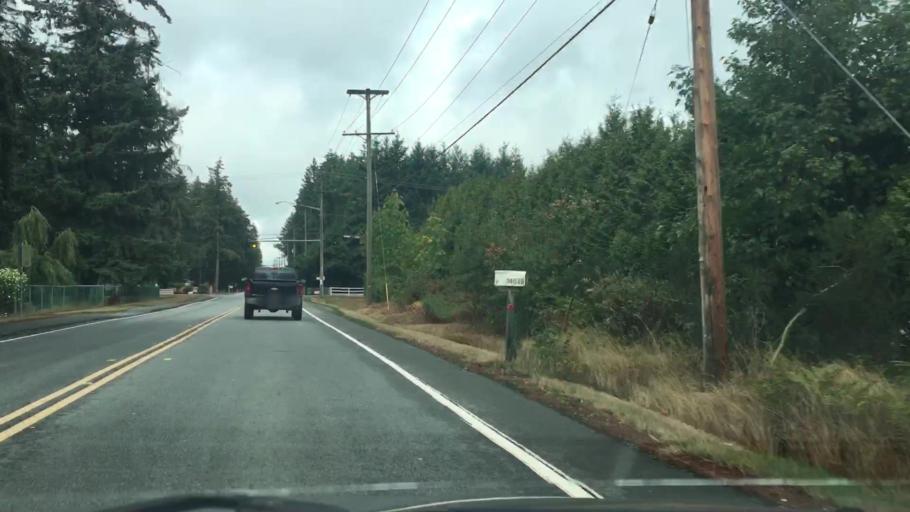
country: CA
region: British Columbia
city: Langley
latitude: 49.1041
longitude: -122.5577
